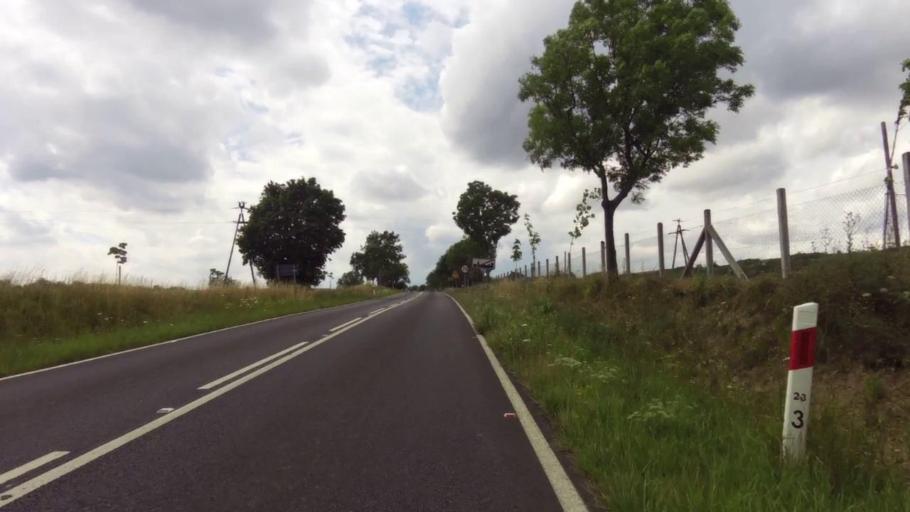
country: PL
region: West Pomeranian Voivodeship
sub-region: Powiat gryfinski
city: Moryn
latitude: 52.8608
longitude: 14.3801
